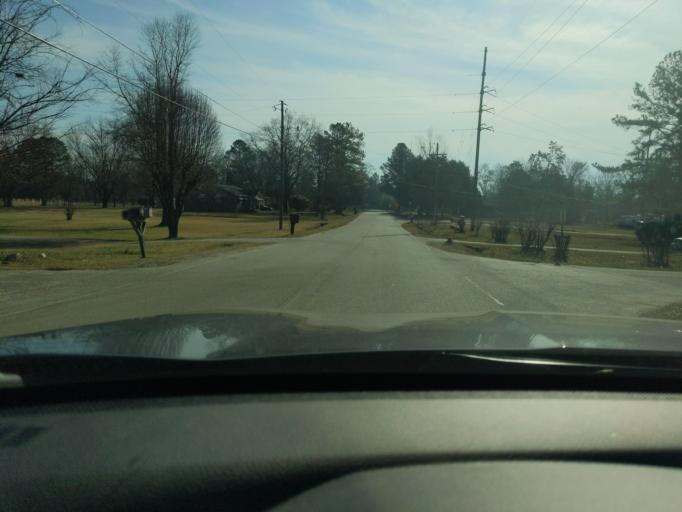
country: US
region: South Carolina
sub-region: Abbeville County
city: Calhoun Falls
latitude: 34.0858
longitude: -82.5830
